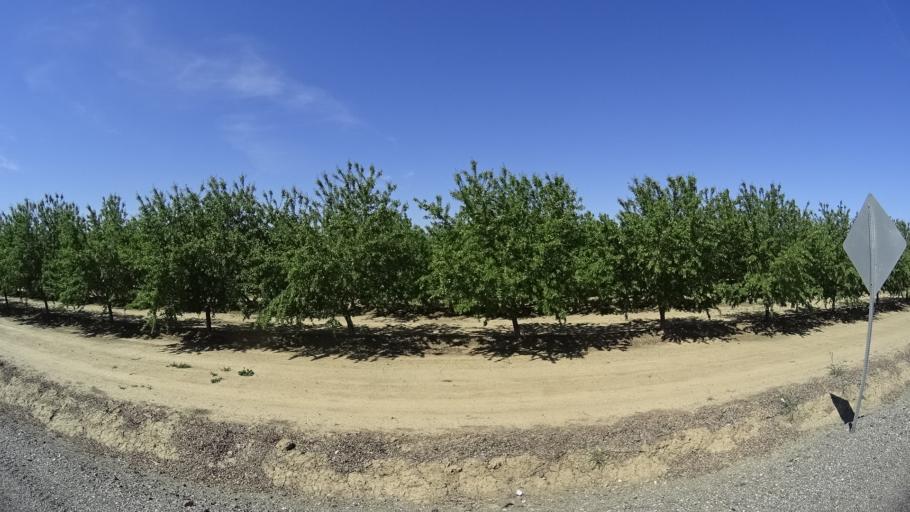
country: US
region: California
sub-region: Glenn County
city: Willows
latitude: 39.6252
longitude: -122.1415
